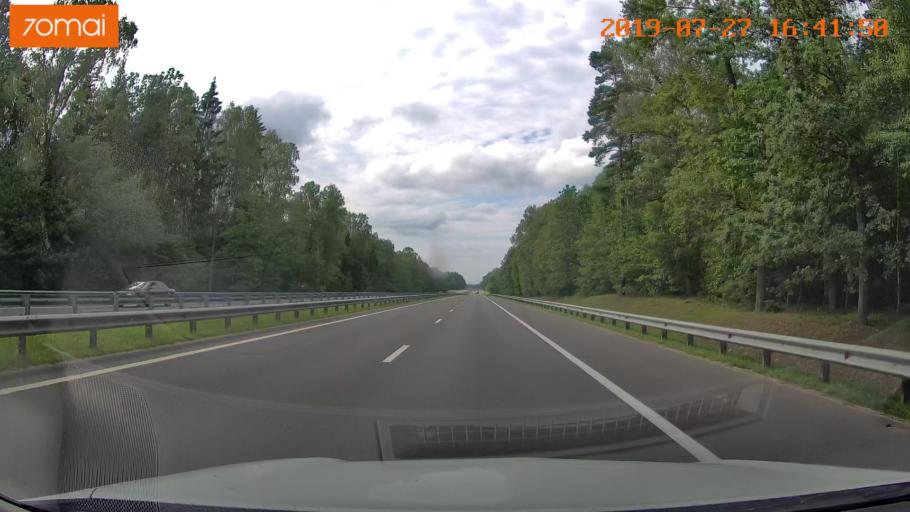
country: RU
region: Kaliningrad
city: Gvardeysk
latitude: 54.6591
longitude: 21.1385
